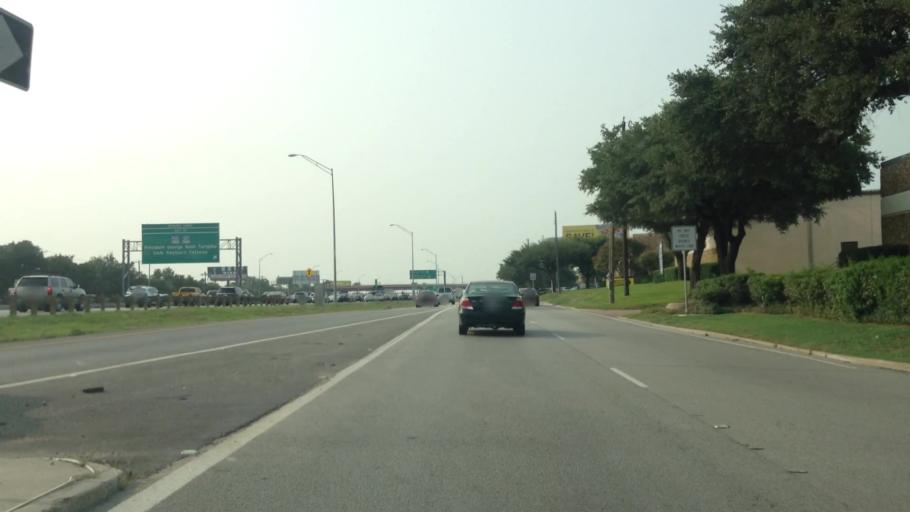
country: US
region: Texas
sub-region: Dallas County
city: Carrollton
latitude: 32.9601
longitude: -96.9142
